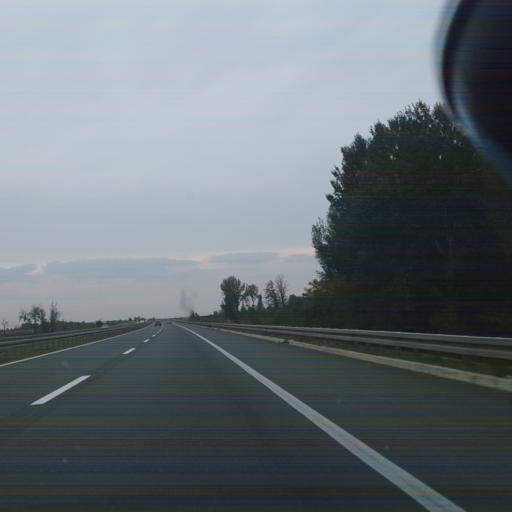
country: RS
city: Beska
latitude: 45.1884
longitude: 20.0768
